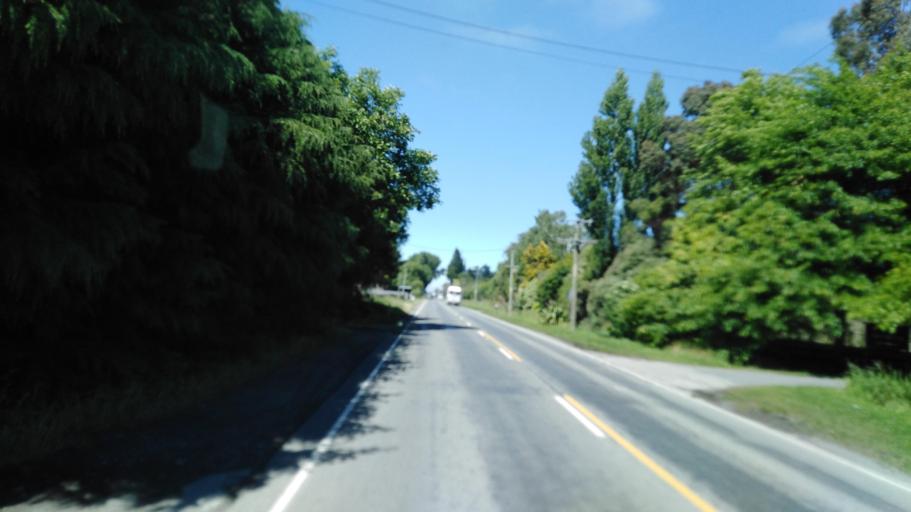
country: NZ
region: Canterbury
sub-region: Selwyn District
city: Prebbleton
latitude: -43.5211
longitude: 172.5039
